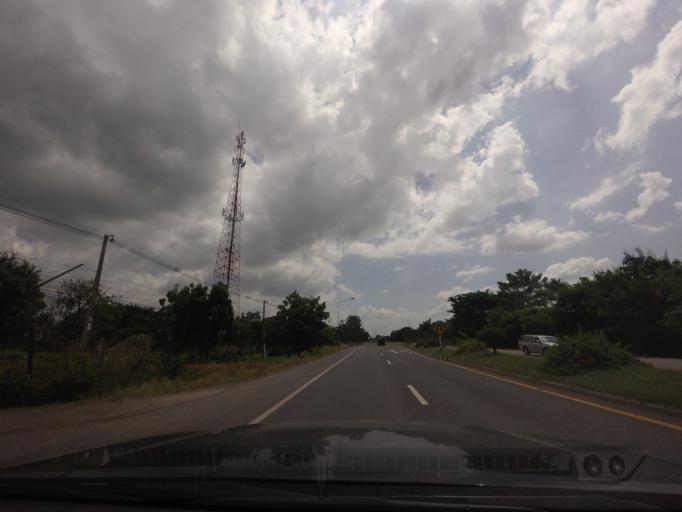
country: TH
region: Phetchabun
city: Nong Phai
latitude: 16.1934
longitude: 101.0889
